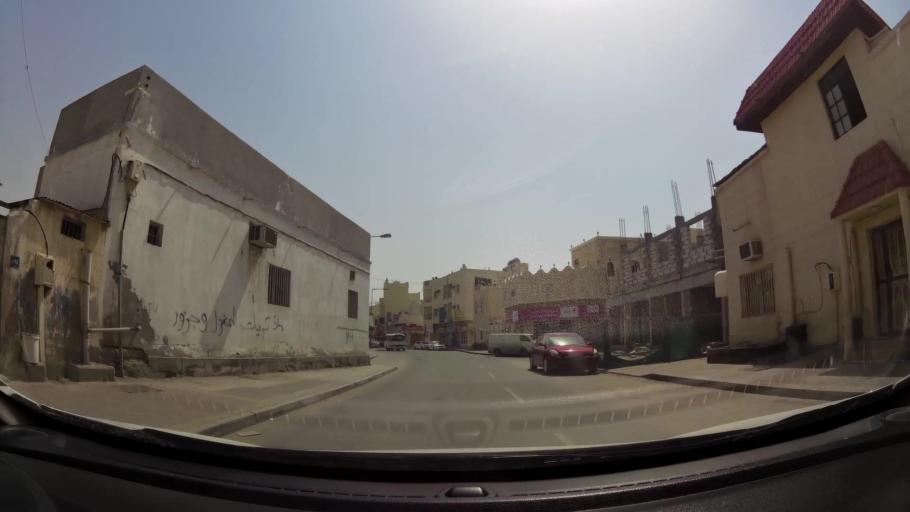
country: BH
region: Manama
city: Jidd Hafs
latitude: 26.2153
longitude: 50.4505
